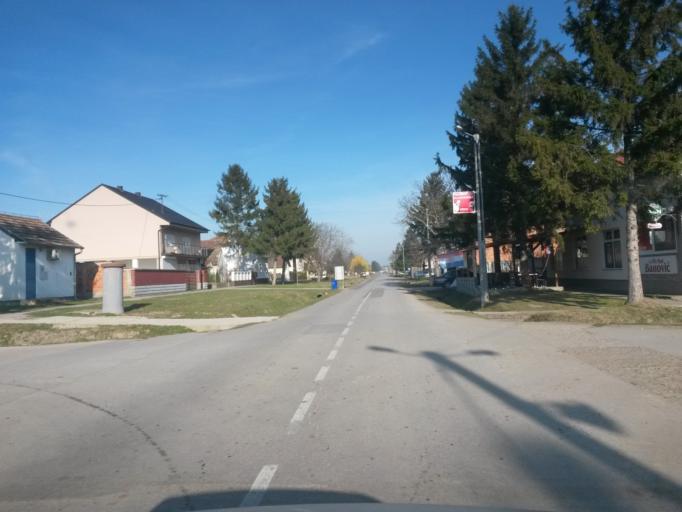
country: HR
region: Vukovarsko-Srijemska
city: Mirkovci
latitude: 45.2396
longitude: 18.8958
